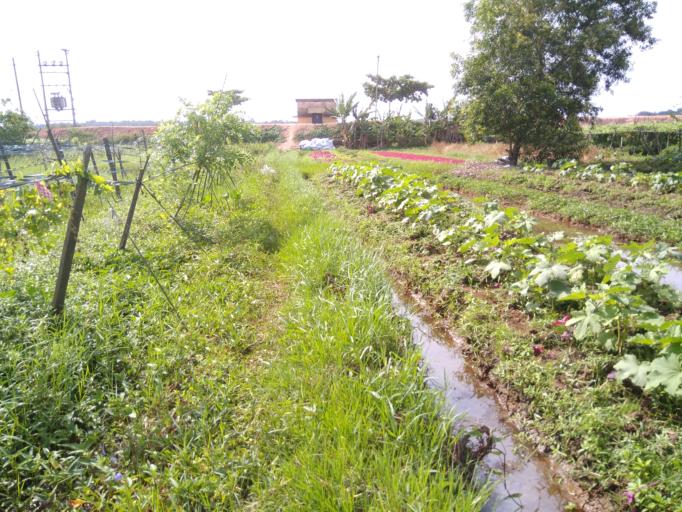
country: IN
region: Kerala
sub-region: Thiruvananthapuram
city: Thiruvananthapuram
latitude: 8.4409
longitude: 76.9827
